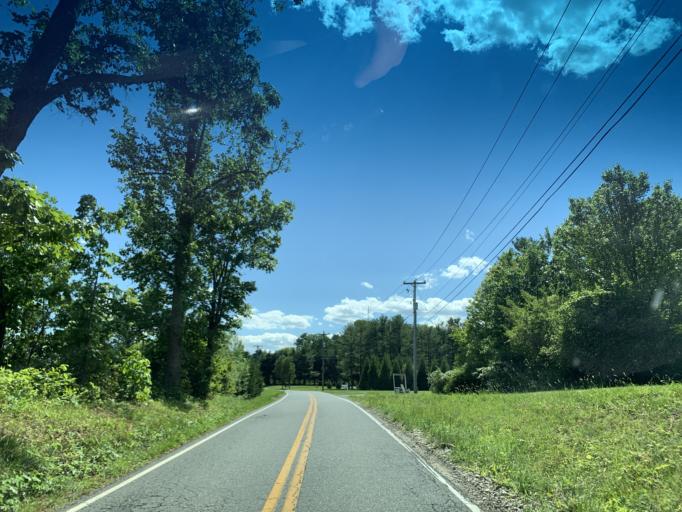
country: US
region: Maryland
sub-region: Cecil County
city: Charlestown
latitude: 39.5158
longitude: -75.9486
